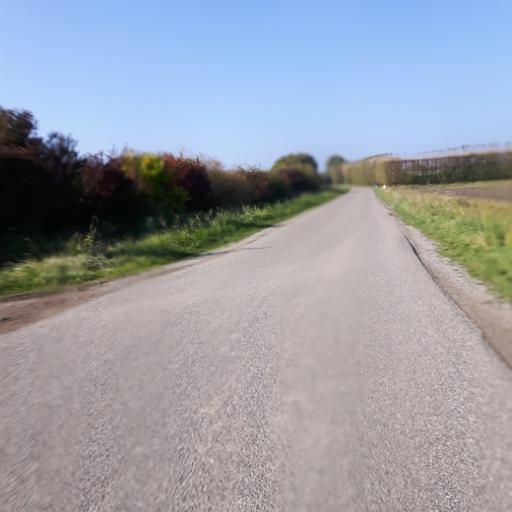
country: NL
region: Zeeland
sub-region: Gemeente Reimerswaal
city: Yerseke
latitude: 51.4868
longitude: 3.9786
